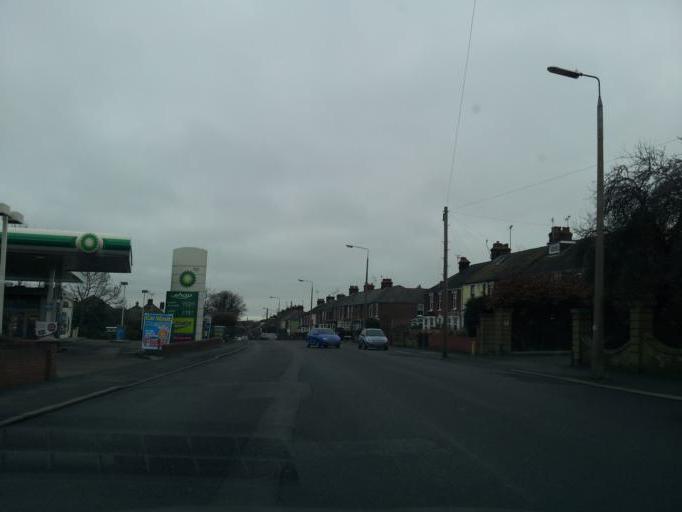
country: GB
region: England
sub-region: Essex
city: Dovercourt
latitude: 51.9350
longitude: 1.2672
